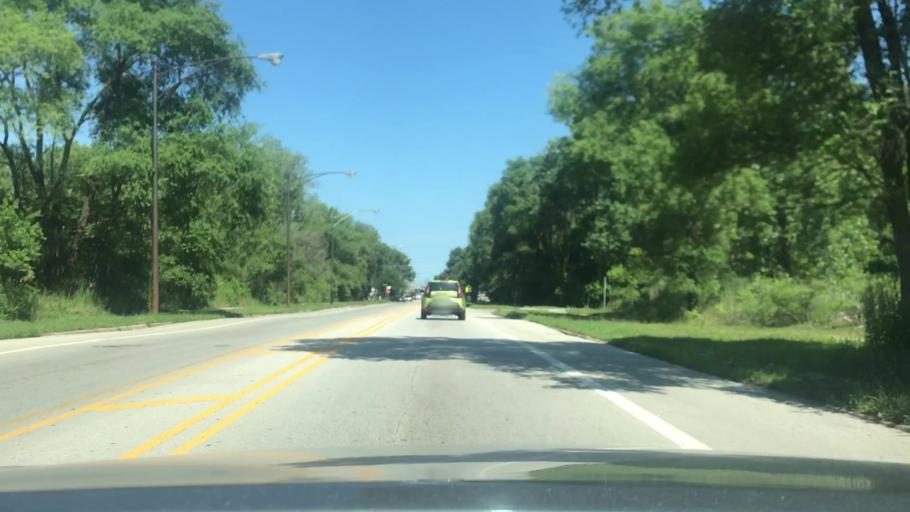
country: US
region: Indiana
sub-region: Lake County
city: Whiting
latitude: 41.7134
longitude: -87.5559
